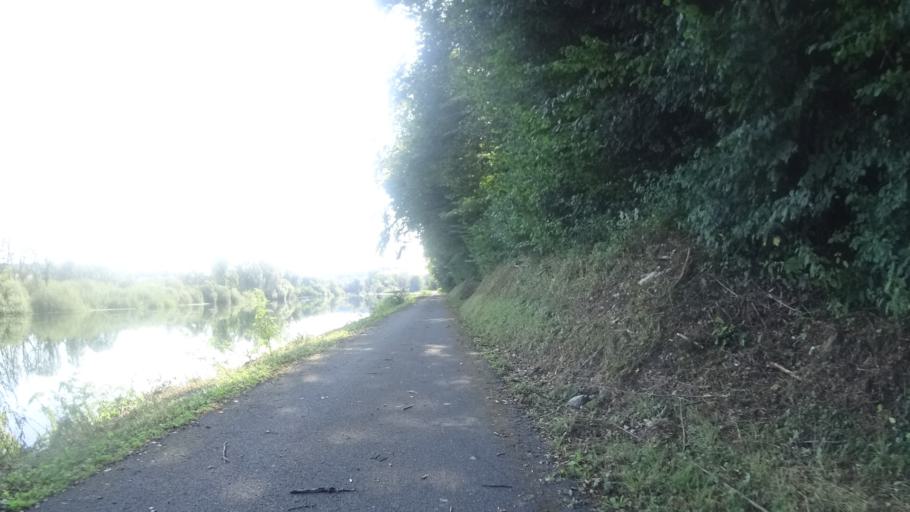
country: FR
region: Franche-Comte
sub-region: Departement du Doubs
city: Clerval
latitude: 47.4277
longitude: 6.5437
